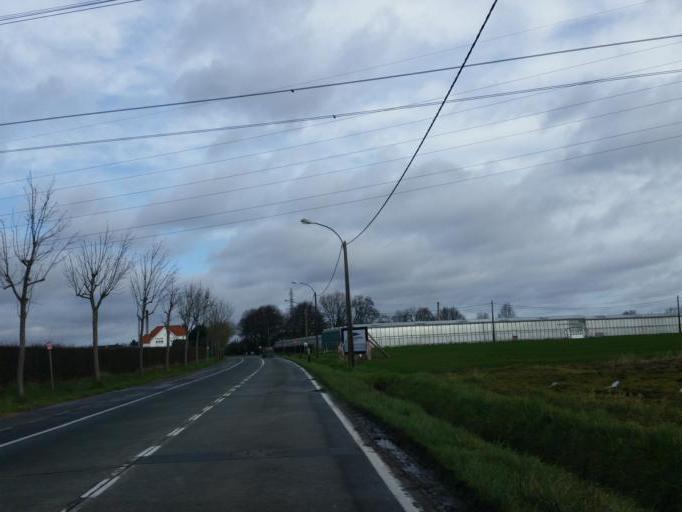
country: BE
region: Flanders
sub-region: Provincie Antwerpen
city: Lint
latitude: 51.1152
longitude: 4.4772
